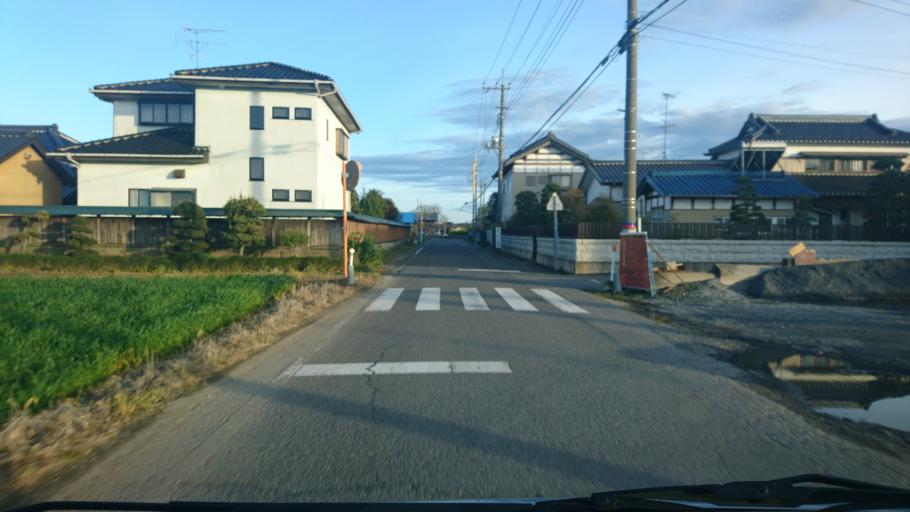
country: JP
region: Ibaraki
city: Ishige
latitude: 36.0985
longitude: 139.9942
